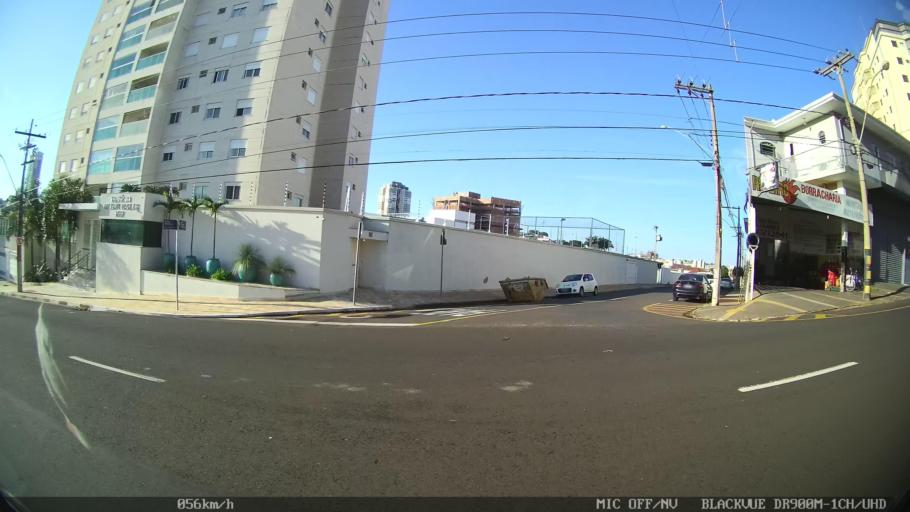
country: BR
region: Sao Paulo
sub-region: Franca
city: Franca
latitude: -20.5388
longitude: -47.3891
